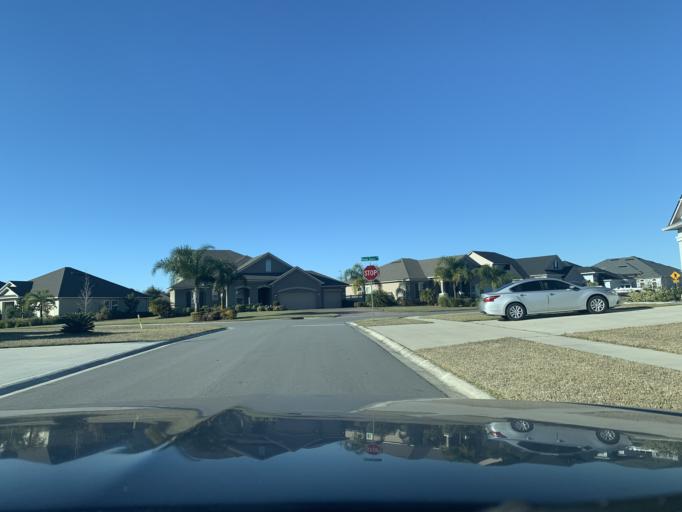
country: US
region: Florida
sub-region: Clay County
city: Green Cove Springs
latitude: 29.9779
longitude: -81.5250
